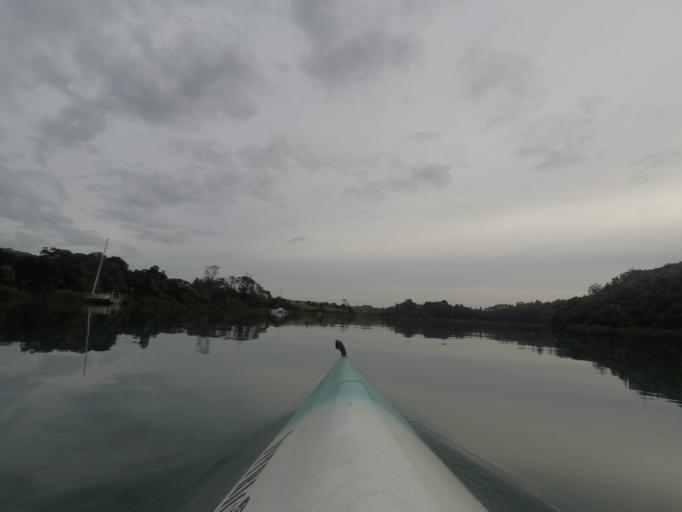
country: NZ
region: Auckland
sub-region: Auckland
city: Rothesay Bay
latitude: -36.6733
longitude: 174.7175
